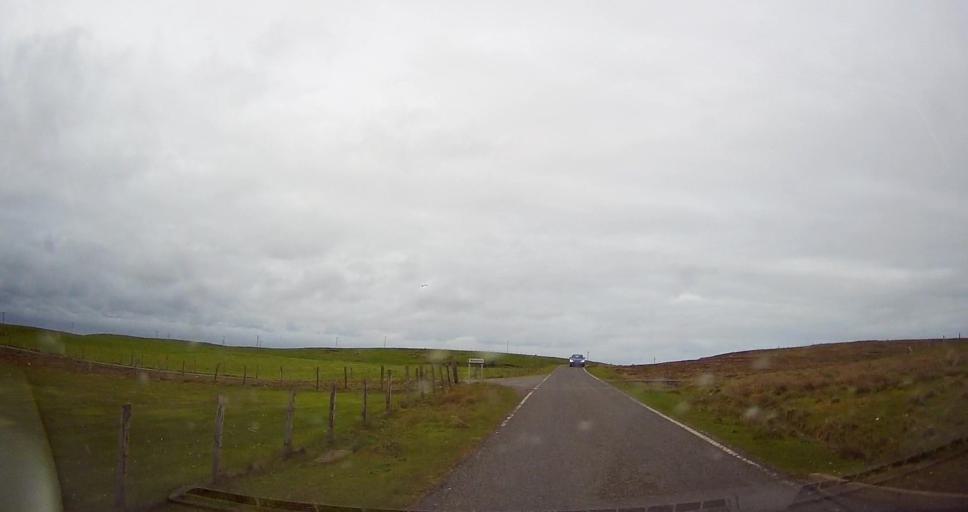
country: GB
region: Scotland
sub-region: Shetland Islands
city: Lerwick
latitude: 60.4940
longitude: -1.5595
